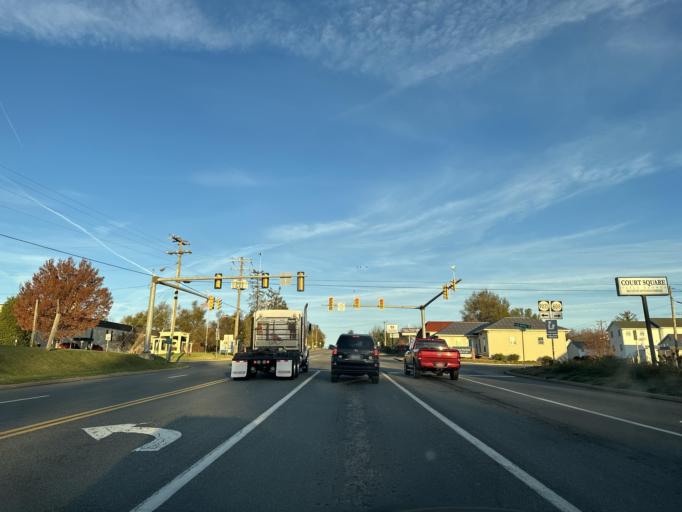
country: US
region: Virginia
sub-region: Augusta County
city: Fishersville
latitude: 38.0987
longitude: -78.9689
